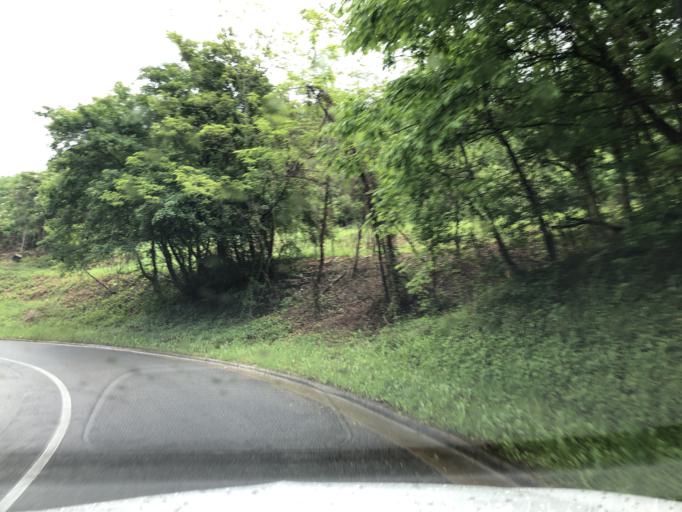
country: SI
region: Koper-Capodistria
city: Prade
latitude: 45.5025
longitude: 13.7727
